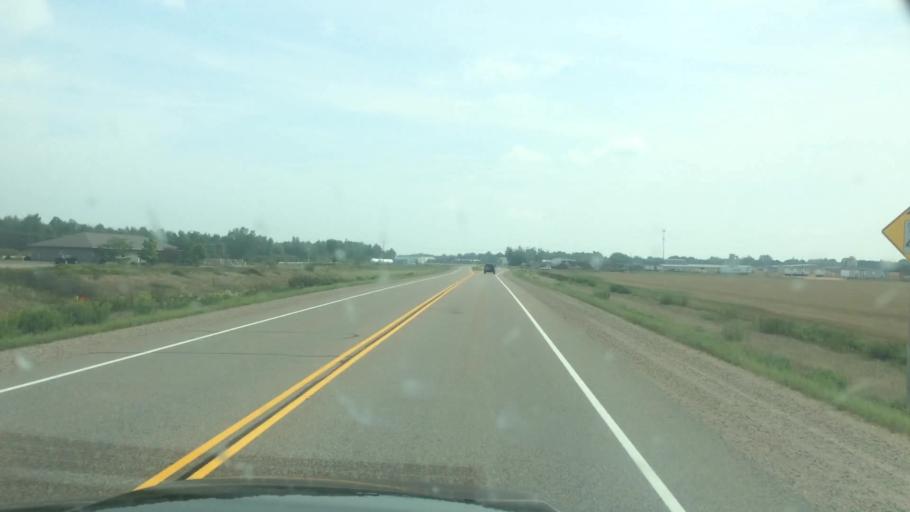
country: US
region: Wisconsin
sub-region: Langlade County
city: Antigo
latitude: 45.1540
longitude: -89.1725
